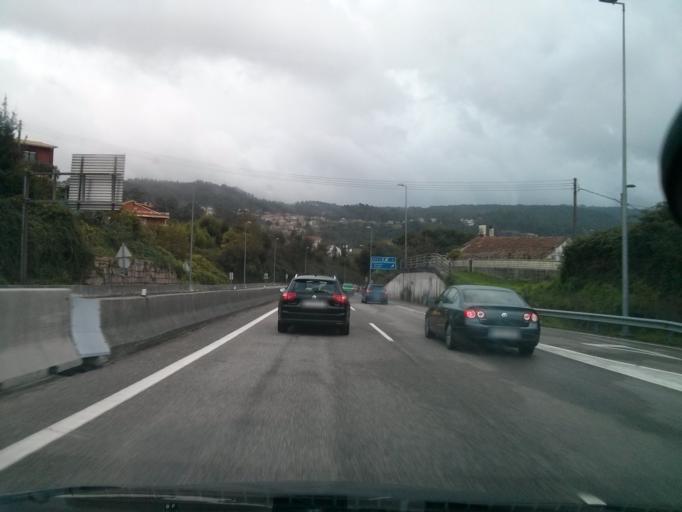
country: ES
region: Galicia
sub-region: Provincia de Pontevedra
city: Vigo
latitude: 42.2106
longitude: -8.6906
